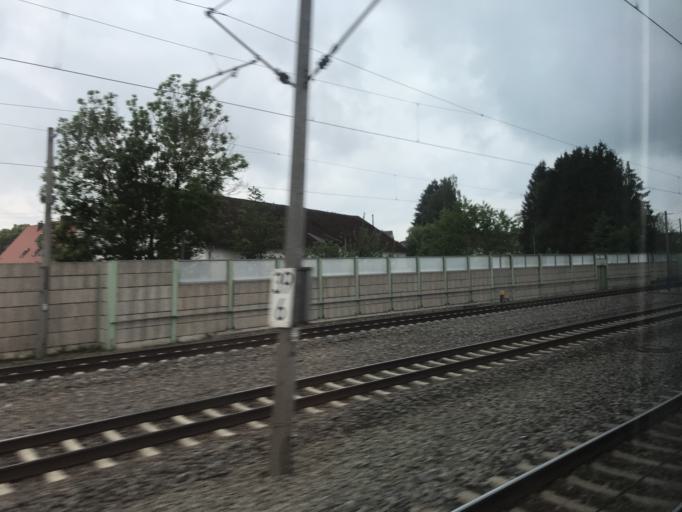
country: DE
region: Bavaria
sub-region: Upper Bavaria
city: Althegnenberg
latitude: 48.2356
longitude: 11.0657
